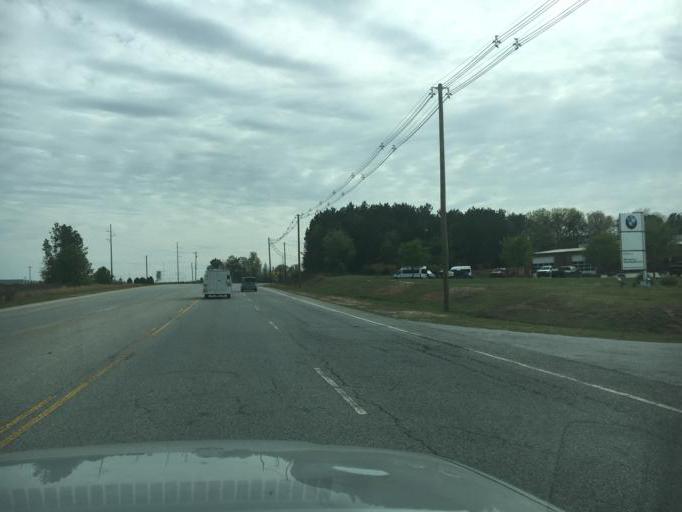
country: US
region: South Carolina
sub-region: Greenville County
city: Greer
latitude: 34.9013
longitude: -82.1930
